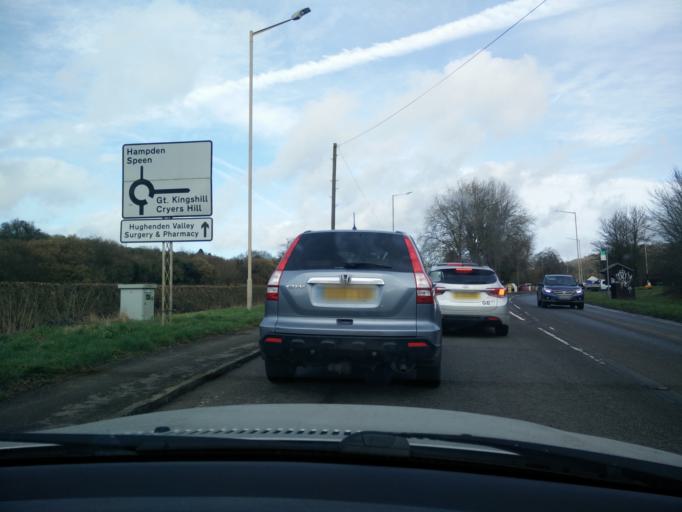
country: GB
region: England
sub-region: Buckinghamshire
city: High Wycombe
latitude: 51.6585
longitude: -0.7511
